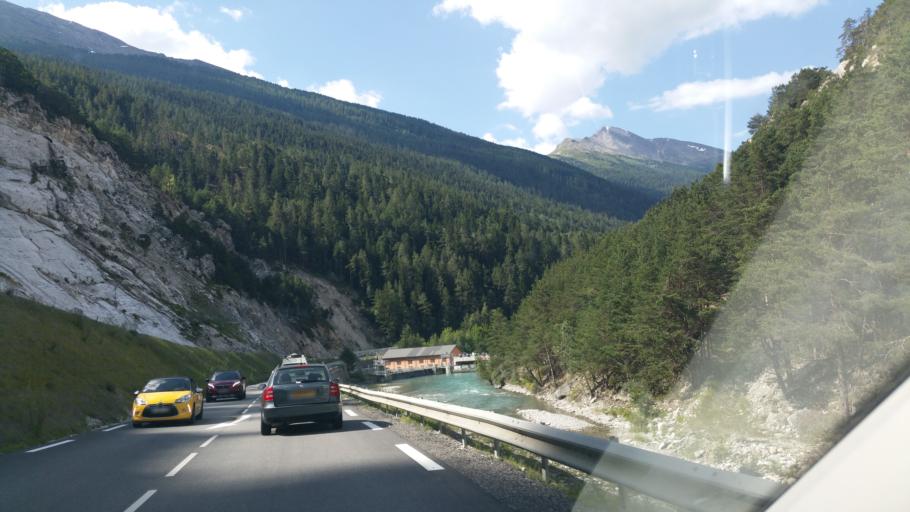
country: FR
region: Rhone-Alpes
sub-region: Departement de la Savoie
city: Modane
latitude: 45.2224
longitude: 6.7621
